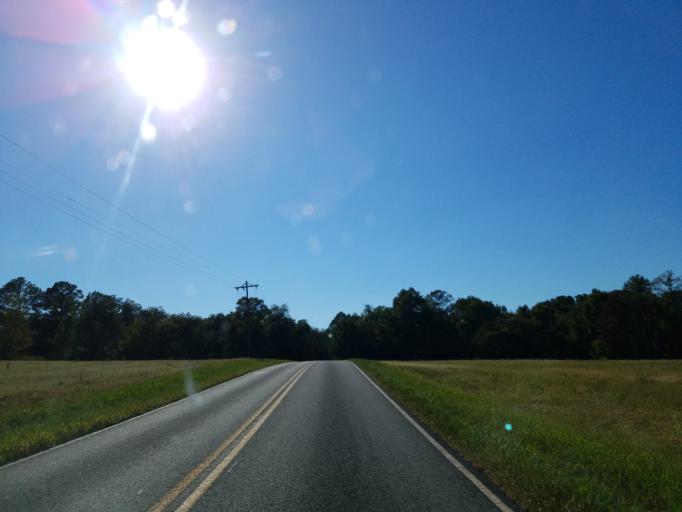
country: US
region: Georgia
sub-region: Dooly County
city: Unadilla
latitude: 32.2443
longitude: -83.8023
